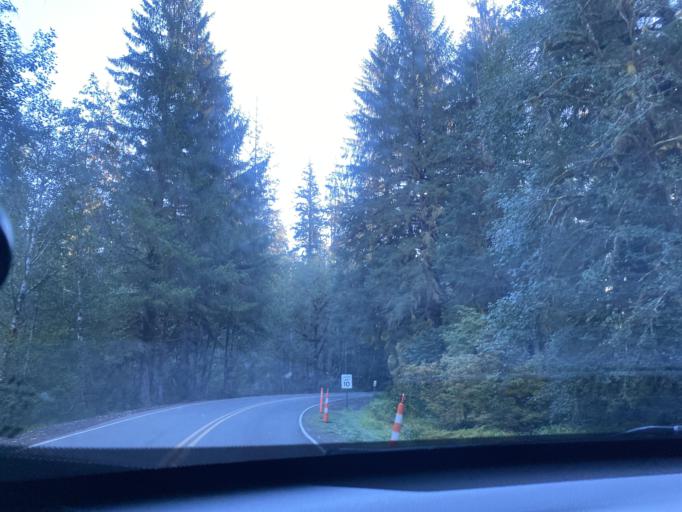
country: US
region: Washington
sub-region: Clallam County
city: Forks
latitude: 47.8607
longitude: -123.9366
